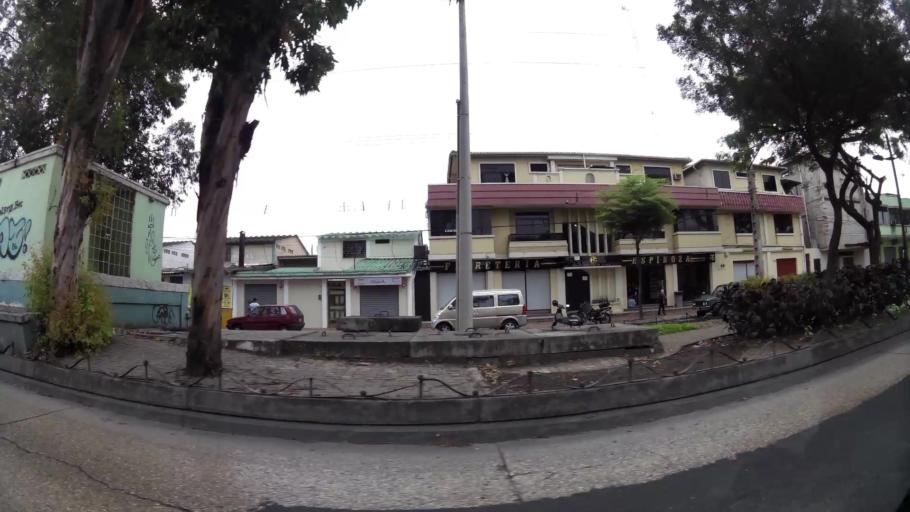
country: EC
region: Guayas
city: Eloy Alfaro
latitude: -2.1375
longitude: -79.9046
